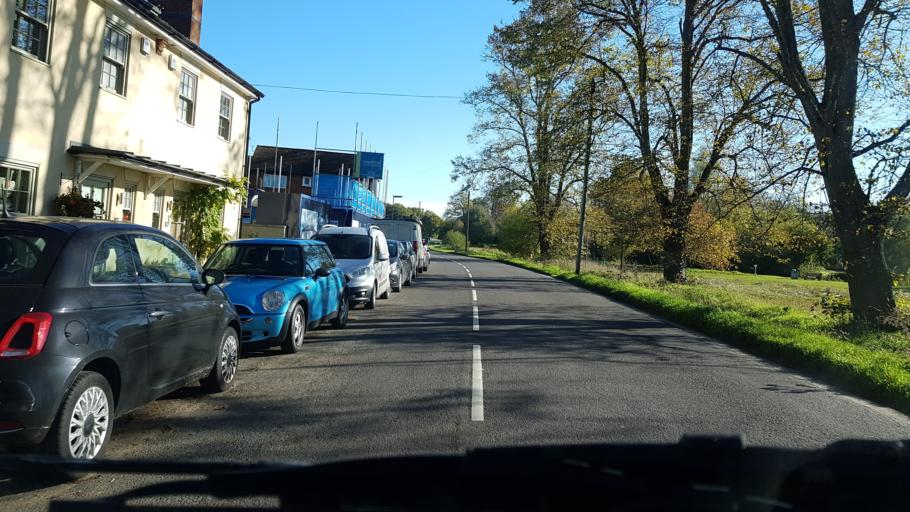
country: GB
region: England
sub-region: Surrey
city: Shalford
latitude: 51.2131
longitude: -0.5658
